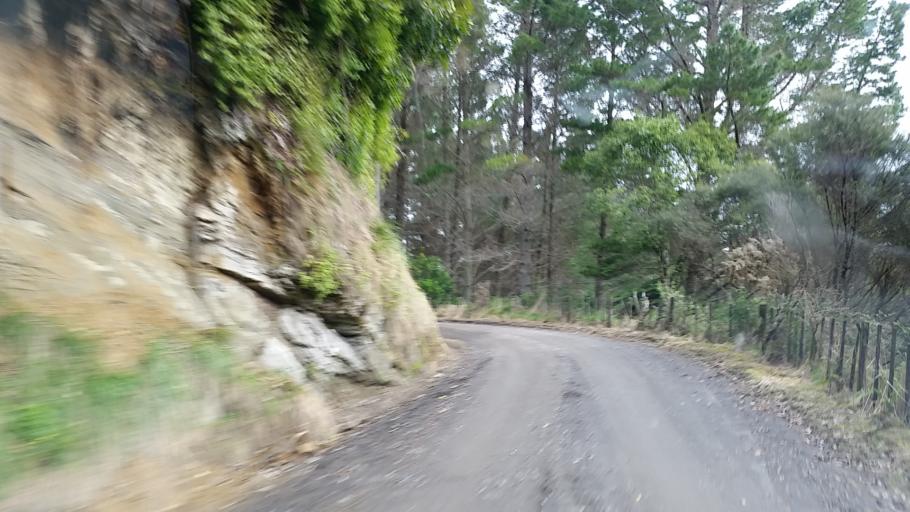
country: NZ
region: Taranaki
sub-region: New Plymouth District
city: Waitara
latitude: -39.1617
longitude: 174.5396
